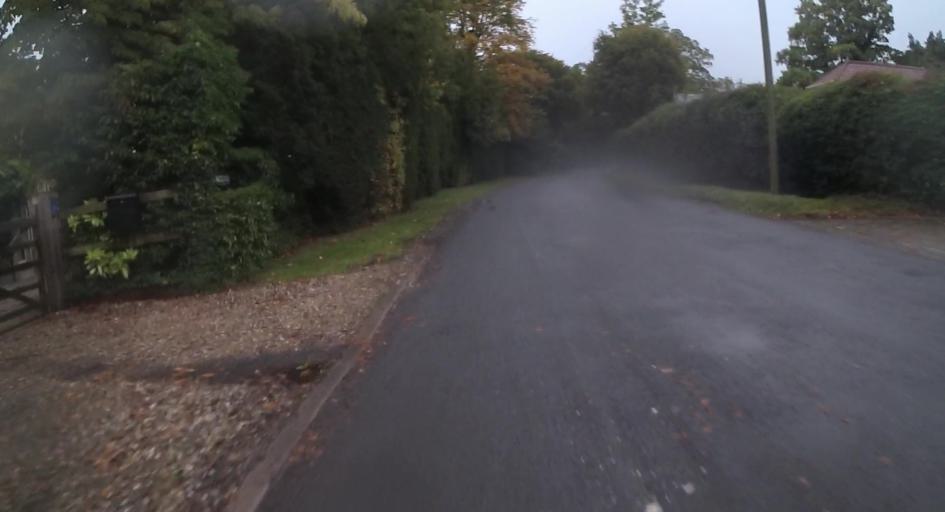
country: GB
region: England
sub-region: Hampshire
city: Tadley
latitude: 51.3035
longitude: -1.1275
